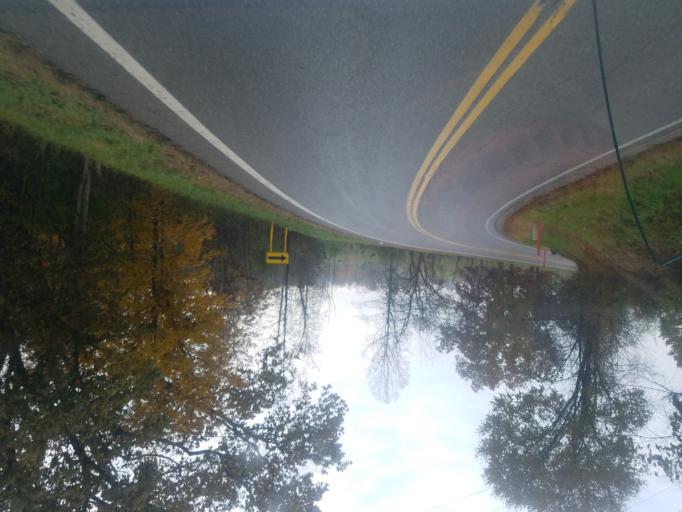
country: US
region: Ohio
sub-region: Morgan County
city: McConnelsville
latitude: 39.4739
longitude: -81.8789
